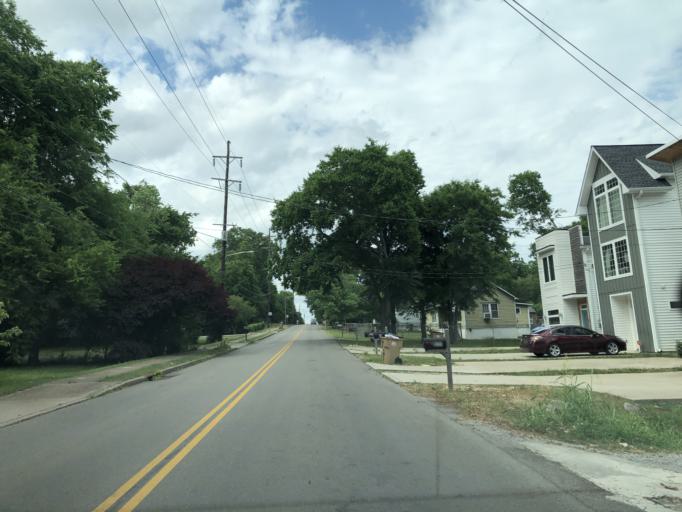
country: US
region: Tennessee
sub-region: Davidson County
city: Goodlettsville
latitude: 36.2683
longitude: -86.7034
